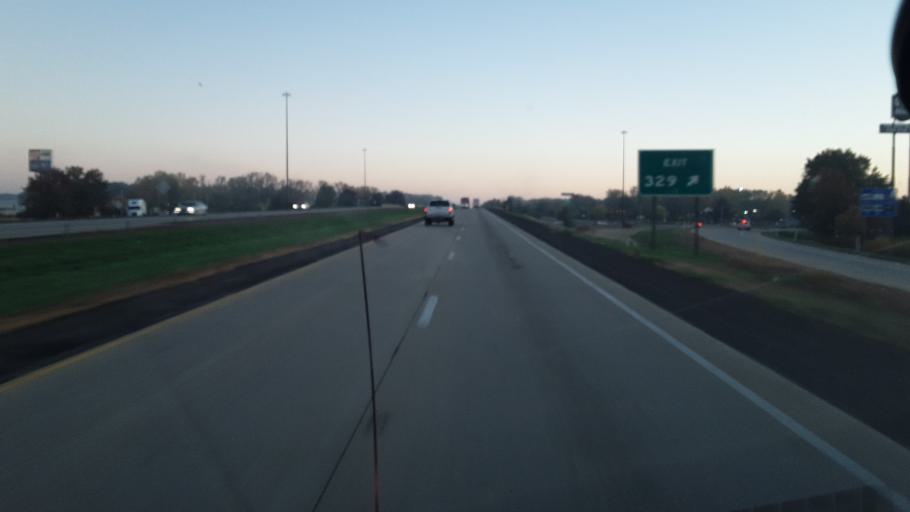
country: US
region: Indiana
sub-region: DeKalb County
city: Auburn
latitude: 41.3640
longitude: -85.0829
